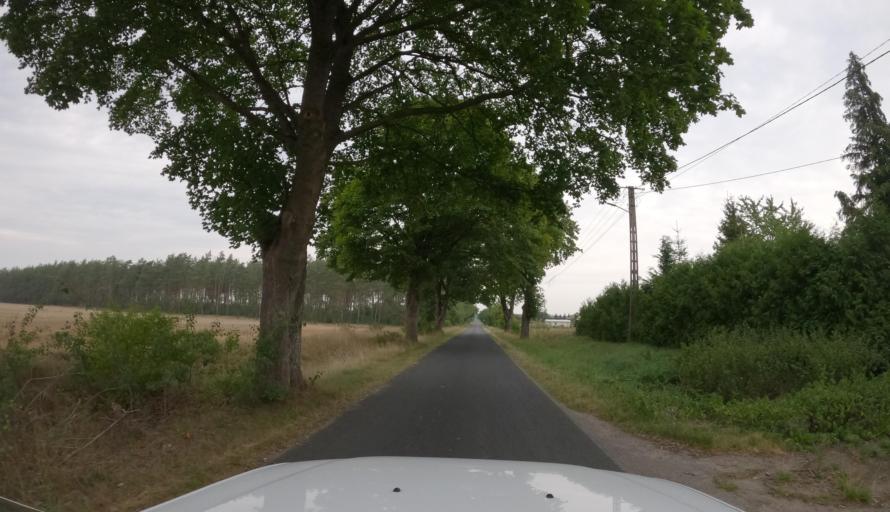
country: PL
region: West Pomeranian Voivodeship
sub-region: Powiat swidwinski
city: Slawoborze
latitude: 53.8177
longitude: 15.5984
